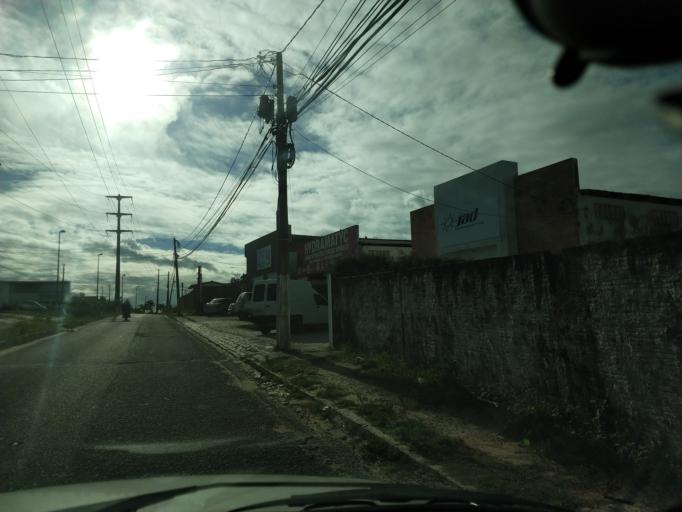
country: BR
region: Rio Grande do Norte
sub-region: Natal
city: Natal
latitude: -5.8472
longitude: -35.2143
